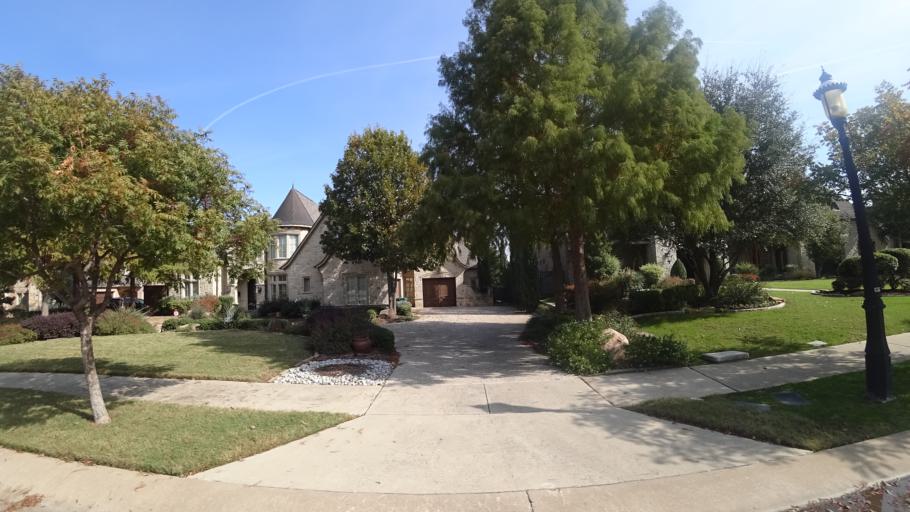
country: US
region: Texas
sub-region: Denton County
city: The Colony
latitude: 33.0405
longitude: -96.8930
